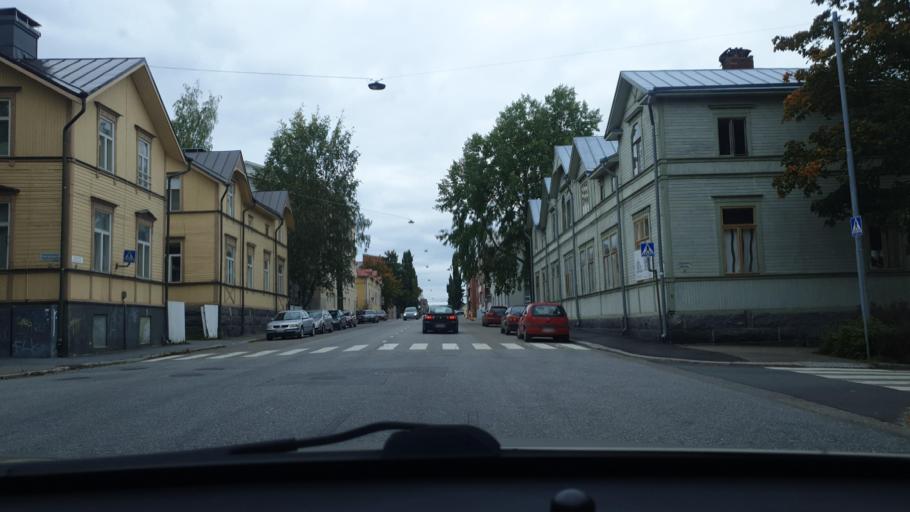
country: FI
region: Ostrobothnia
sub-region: Vaasa
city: Vaasa
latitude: 63.0900
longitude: 21.6275
